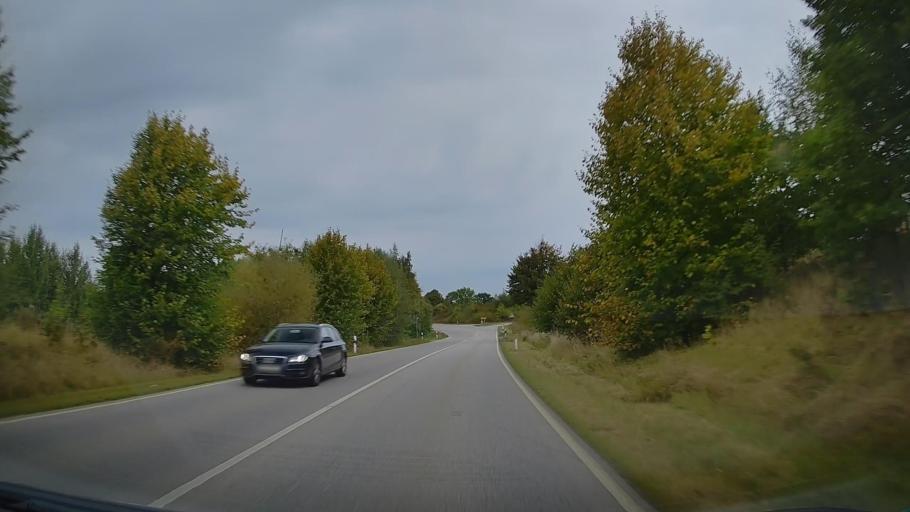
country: DE
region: Schleswig-Holstein
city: Brodersdorf
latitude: 54.3900
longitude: 10.2417
